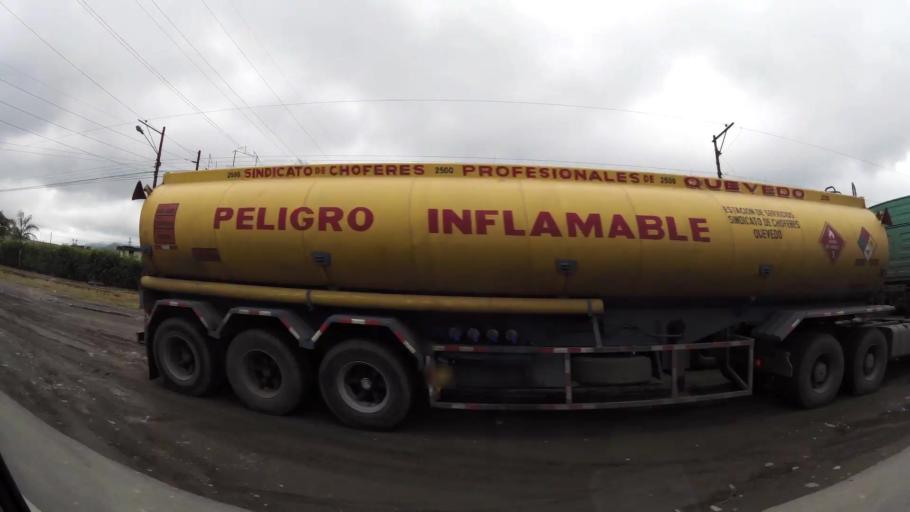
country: EC
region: Santo Domingo de los Tsachilas
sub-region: Canton Santo Domingo de los Colorados
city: Santo Domingo de los Colorados
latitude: -0.2602
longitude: -79.1255
